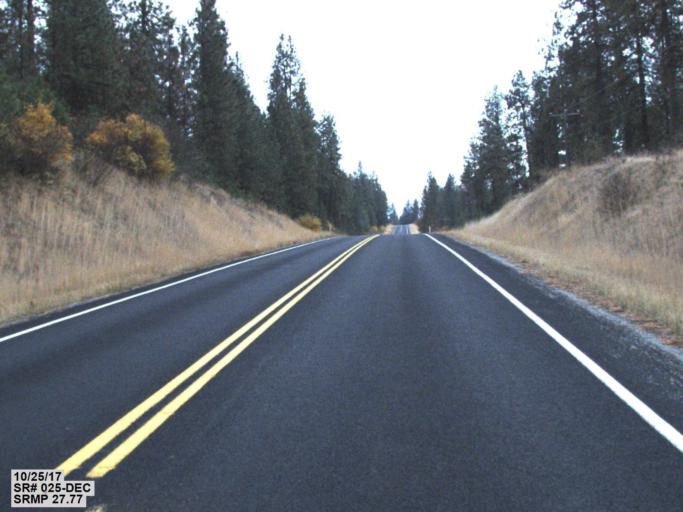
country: US
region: Washington
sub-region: Lincoln County
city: Davenport
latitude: 47.9530
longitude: -118.3120
